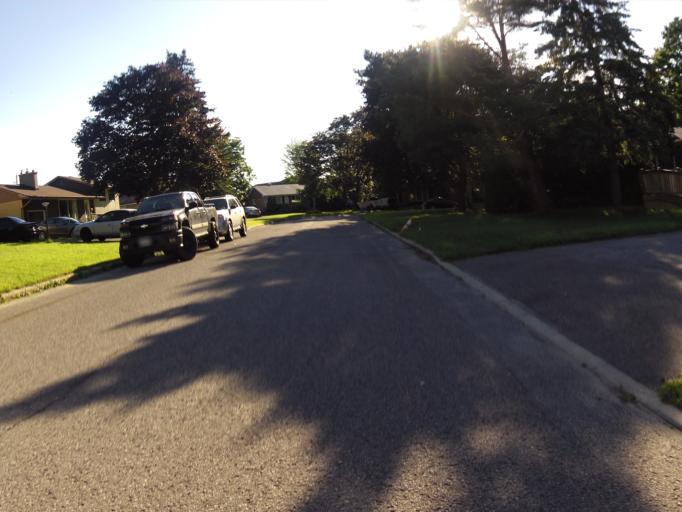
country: CA
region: Ontario
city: Ottawa
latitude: 45.3407
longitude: -75.7363
